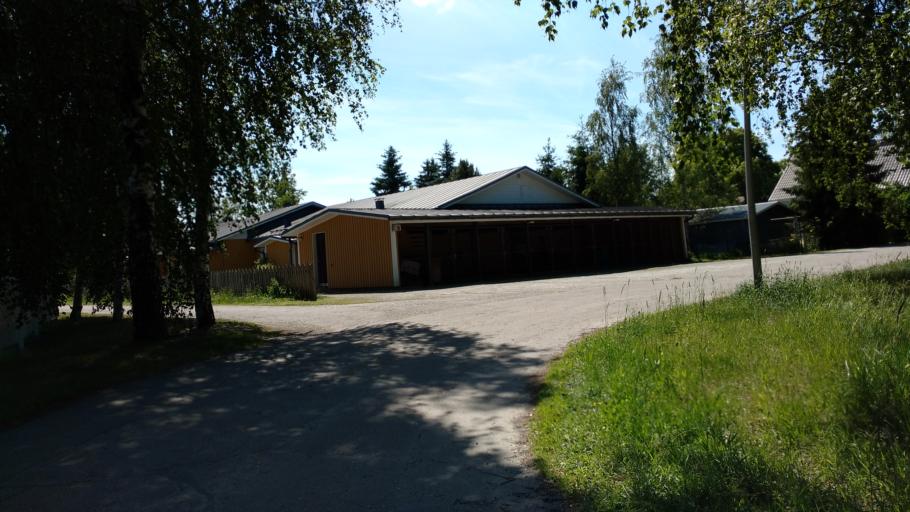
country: FI
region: Varsinais-Suomi
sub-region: Salo
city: Salo
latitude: 60.3936
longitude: 23.1250
